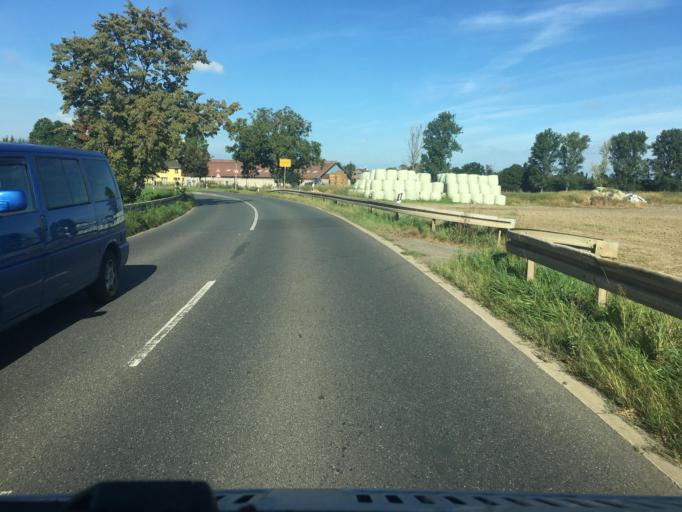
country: DE
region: North Rhine-Westphalia
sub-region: Regierungsbezirk Koln
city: Dueren
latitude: 50.7871
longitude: 6.4440
